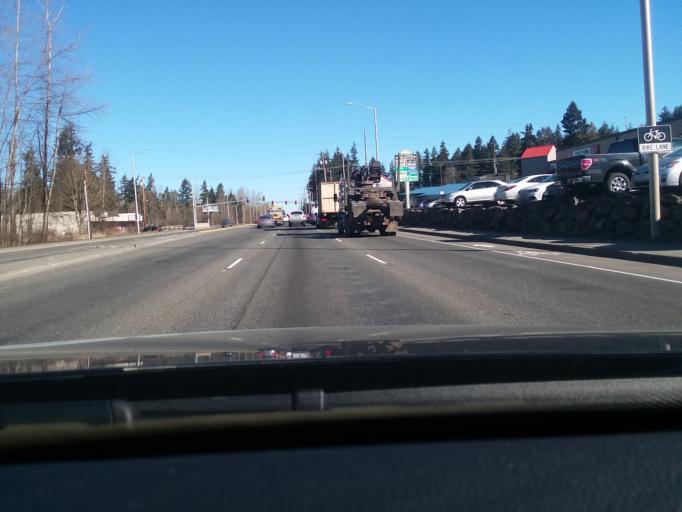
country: US
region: Washington
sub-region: Pierce County
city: Summit
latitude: 47.1384
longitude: -122.3573
